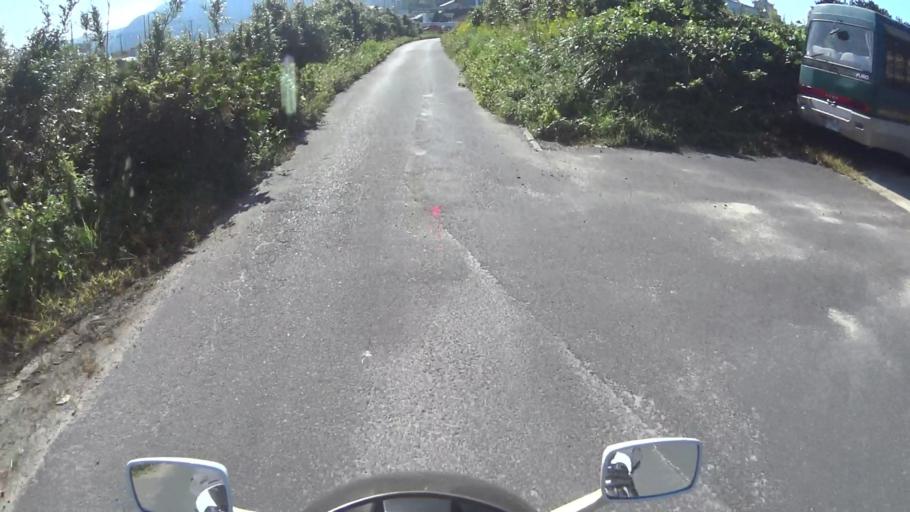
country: JP
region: Kyoto
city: Miyazu
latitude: 35.7471
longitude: 135.1070
